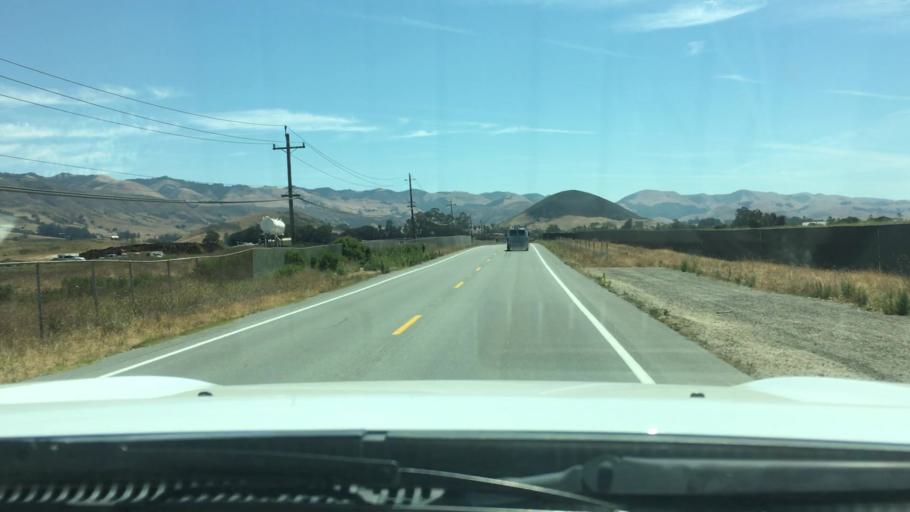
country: US
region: California
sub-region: San Luis Obispo County
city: San Luis Obispo
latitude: 35.2466
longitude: -120.6571
